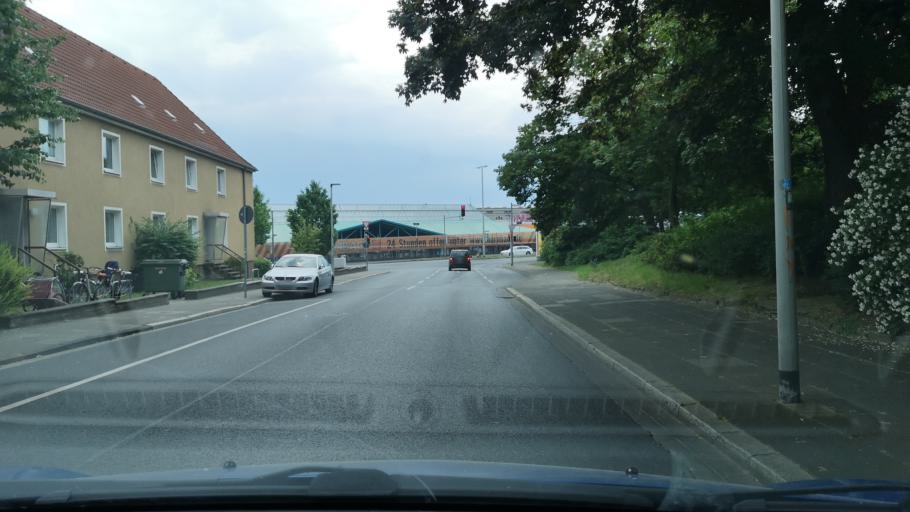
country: DE
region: Lower Saxony
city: Hannover
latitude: 52.3609
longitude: 9.7094
